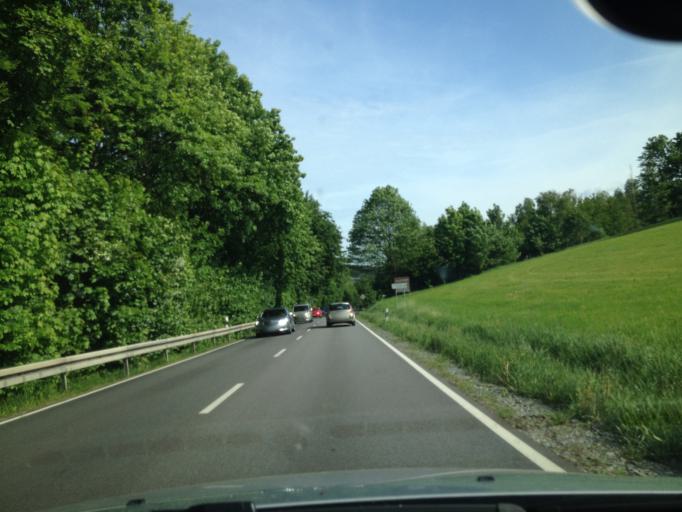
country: DE
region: Saxony
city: Ehrenfriedersdorf
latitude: 50.6385
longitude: 12.9657
